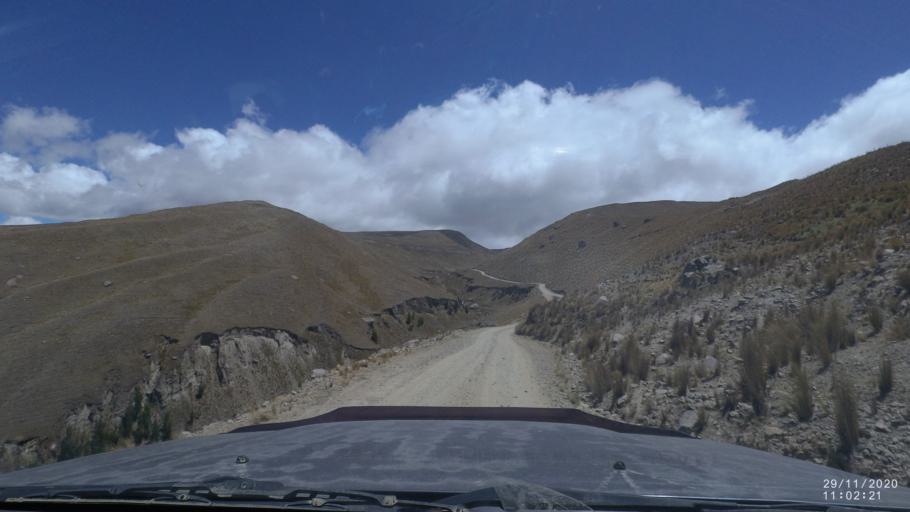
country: BO
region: Cochabamba
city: Cochabamba
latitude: -17.1957
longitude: -66.2257
